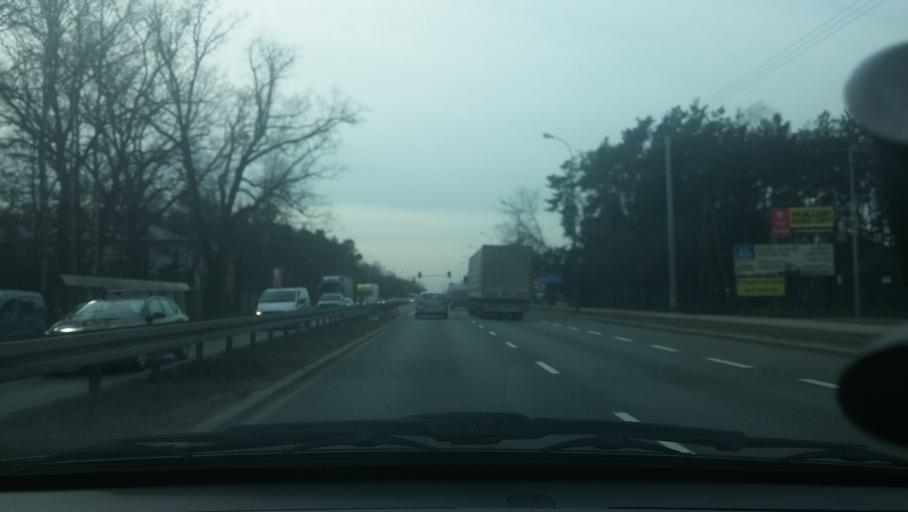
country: PL
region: Masovian Voivodeship
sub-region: Powiat wolominski
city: Slupno
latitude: 52.3541
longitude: 21.1307
